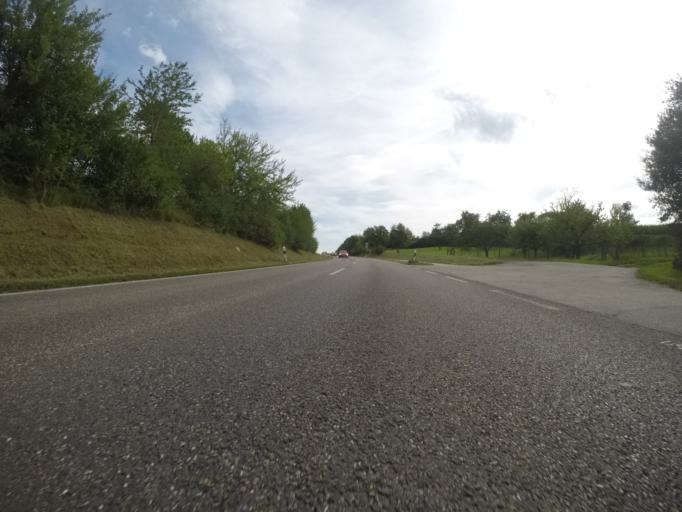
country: DE
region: Baden-Wuerttemberg
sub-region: Regierungsbezirk Stuttgart
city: Rutesheim
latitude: 48.8042
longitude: 8.9408
